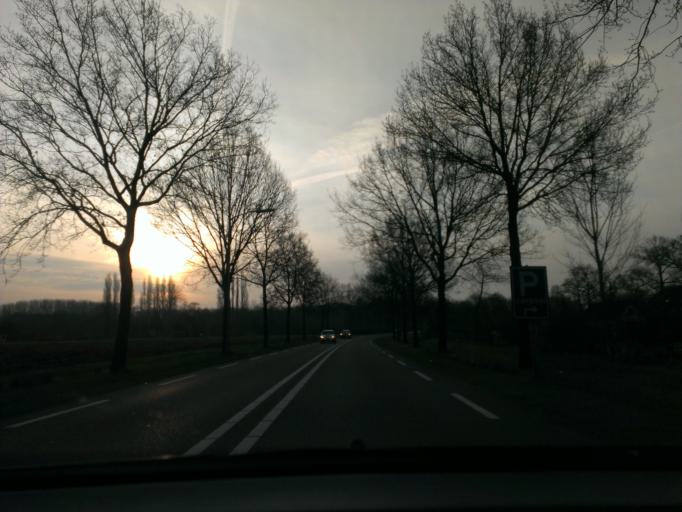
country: NL
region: Gelderland
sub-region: Gemeente Epe
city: Vaassen
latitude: 52.2926
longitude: 6.0026
